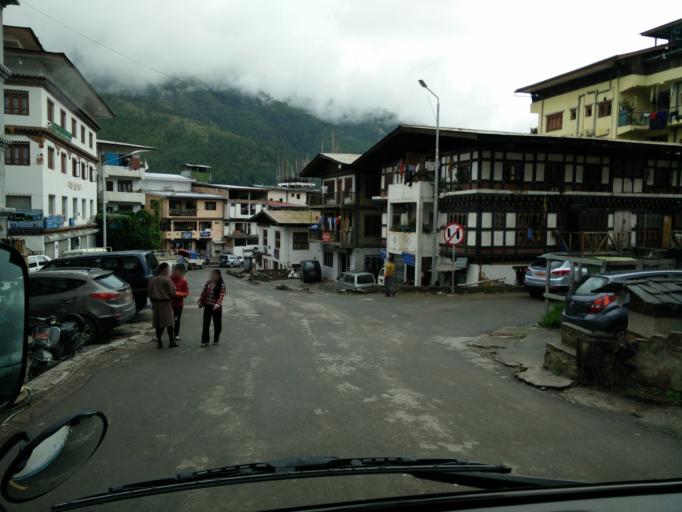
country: BT
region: Thimphu
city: Thimphu
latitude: 27.4731
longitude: 89.6369
